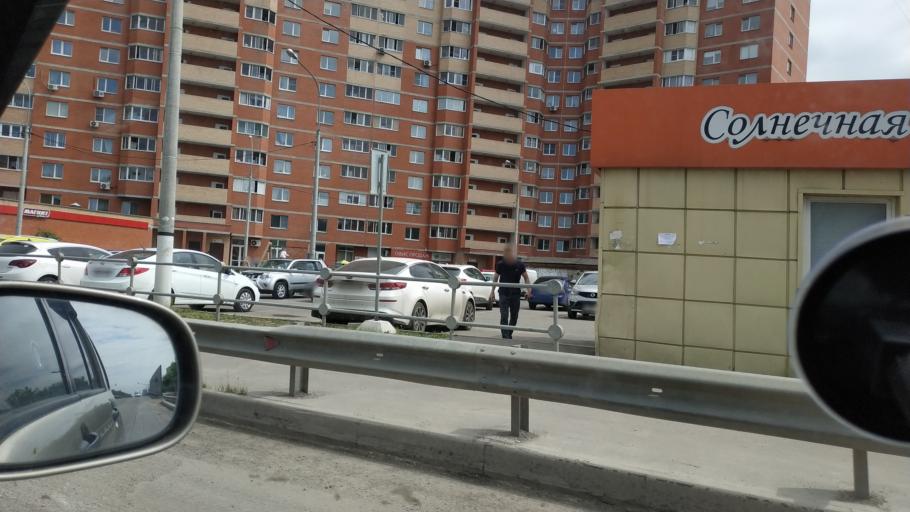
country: RU
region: Moskovskaya
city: Fryazino
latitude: 55.9396
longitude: 38.0328
